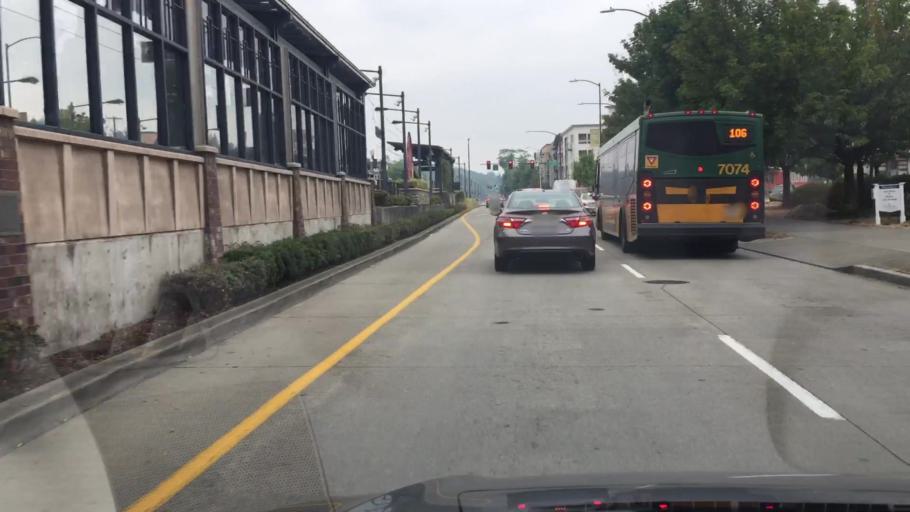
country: US
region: Washington
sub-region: King County
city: Seattle
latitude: 47.5597
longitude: -122.2926
